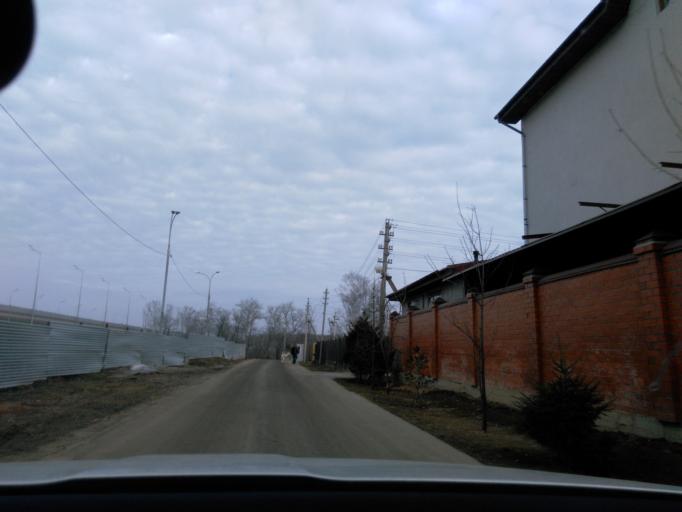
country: RU
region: Moskovskaya
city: Levoberezhnaya
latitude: 55.9072
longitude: 37.4775
